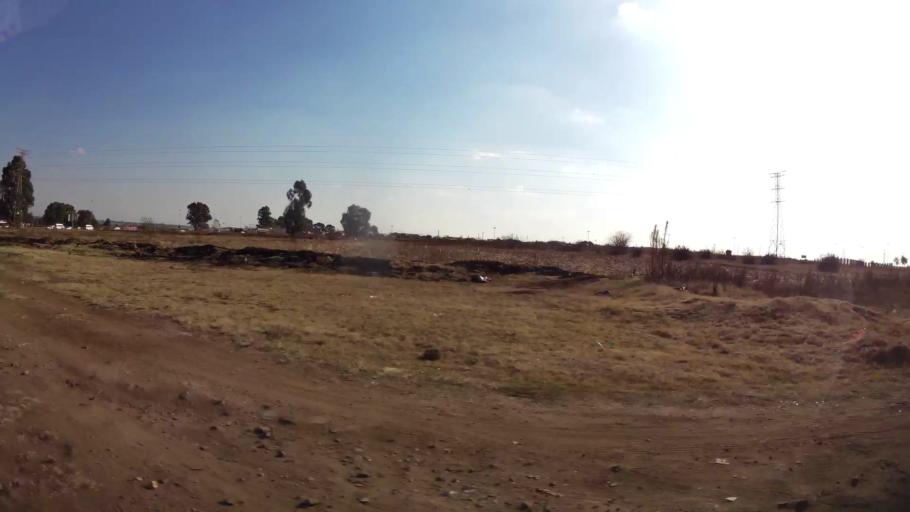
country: ZA
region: Gauteng
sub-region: Ekurhuleni Metropolitan Municipality
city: Brakpan
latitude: -26.1618
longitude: 28.3991
